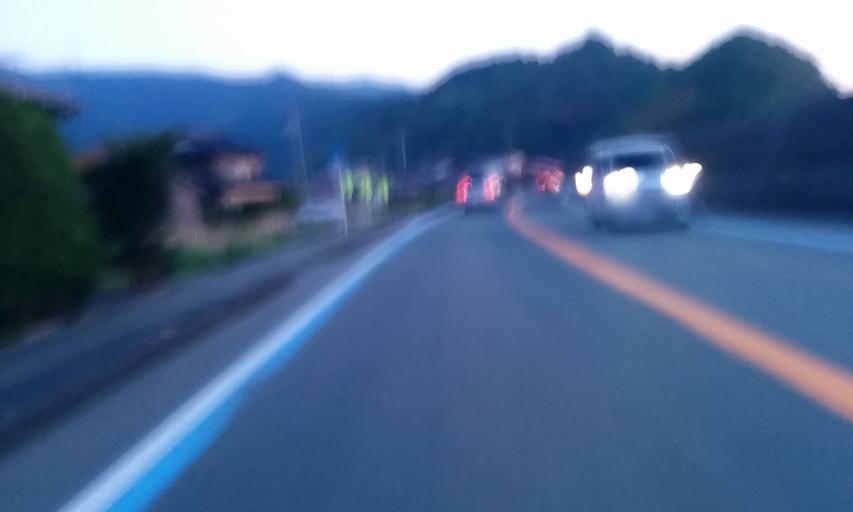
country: JP
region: Ehime
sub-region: Nishiuwa-gun
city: Ikata-cho
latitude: 33.5598
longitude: 132.4339
